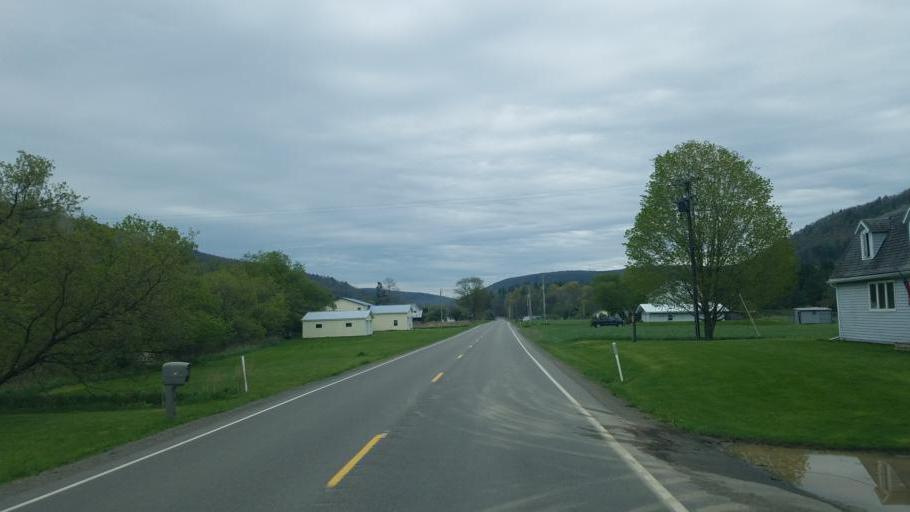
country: US
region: Pennsylvania
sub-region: Tioga County
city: Westfield
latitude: 41.9728
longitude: -77.4593
